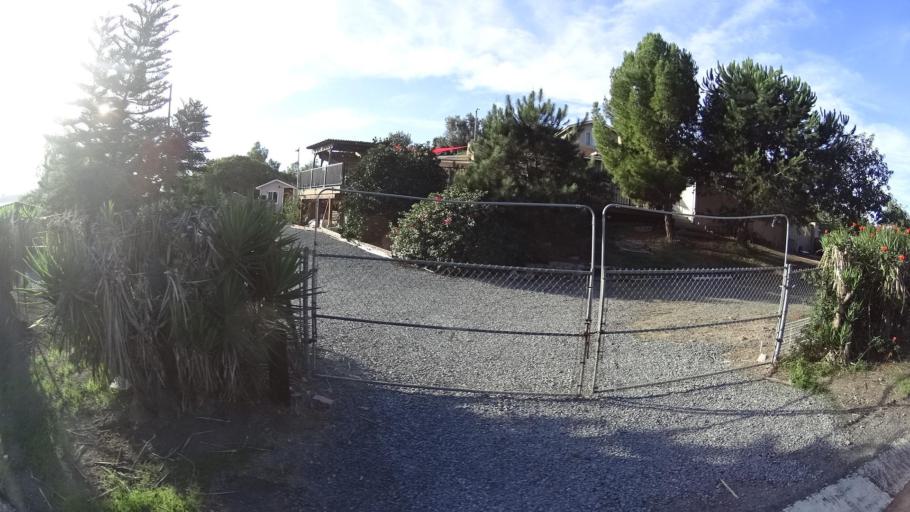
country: US
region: California
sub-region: San Diego County
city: Spring Valley
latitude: 32.7324
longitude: -116.9914
